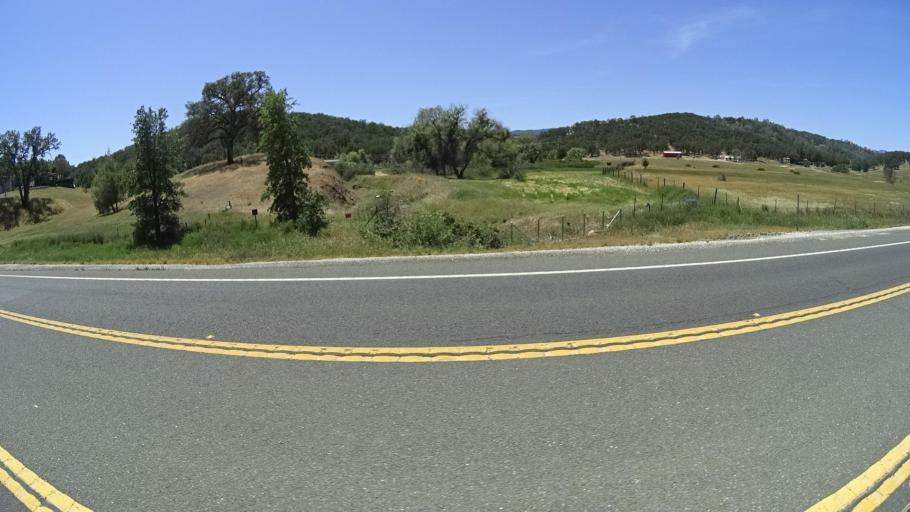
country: US
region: California
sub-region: Lake County
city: Lower Lake
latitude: 38.8905
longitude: -122.6053
